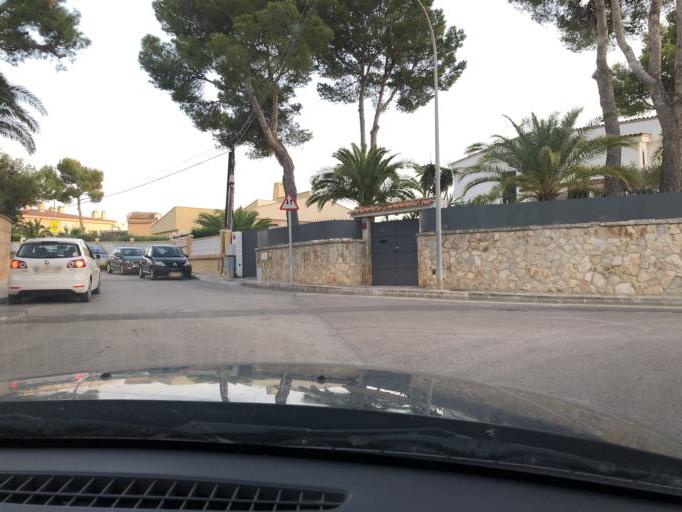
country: ES
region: Balearic Islands
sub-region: Illes Balears
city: Santa Ponsa
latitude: 39.5283
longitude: 2.4697
